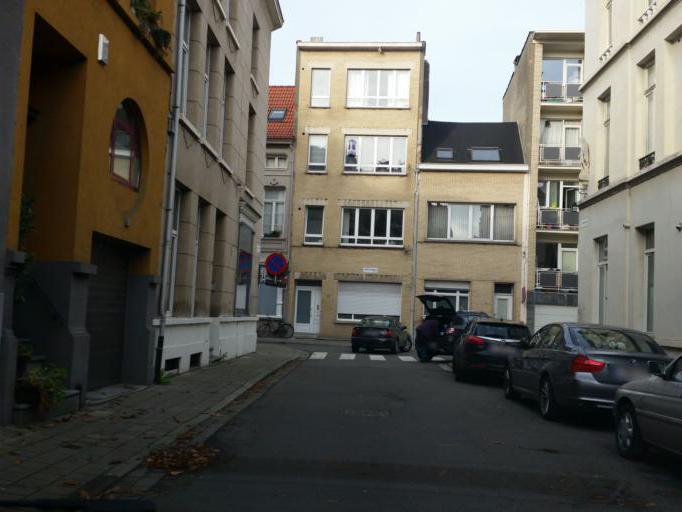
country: BE
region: Flanders
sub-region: Provincie Antwerpen
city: Antwerpen
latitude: 51.2042
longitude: 4.4137
